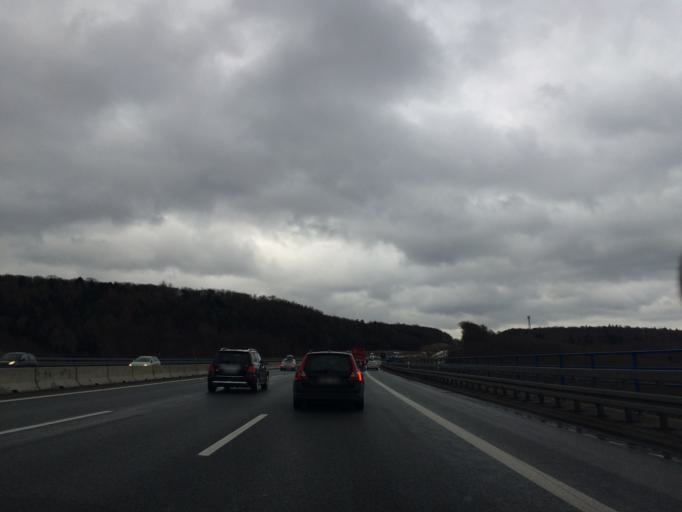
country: DE
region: Bavaria
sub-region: Regierungsbezirk Unterfranken
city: Schollbrunn
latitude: 49.8791
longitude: 9.4371
